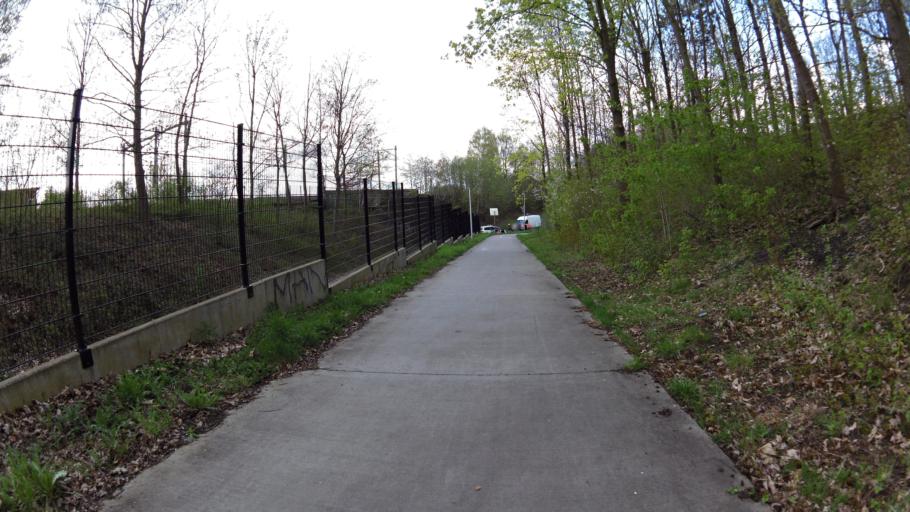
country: NL
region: Limburg
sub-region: Gemeente Heerlen
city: Heerlen
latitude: 50.8956
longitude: 5.9604
